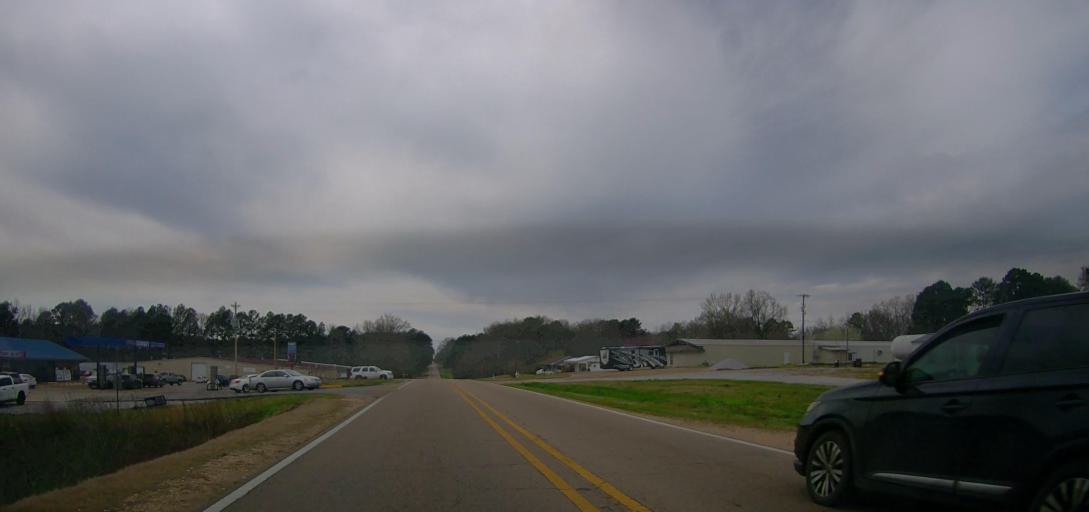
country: US
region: Mississippi
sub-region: Itawamba County
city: Mantachie
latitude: 34.2551
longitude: -88.4908
